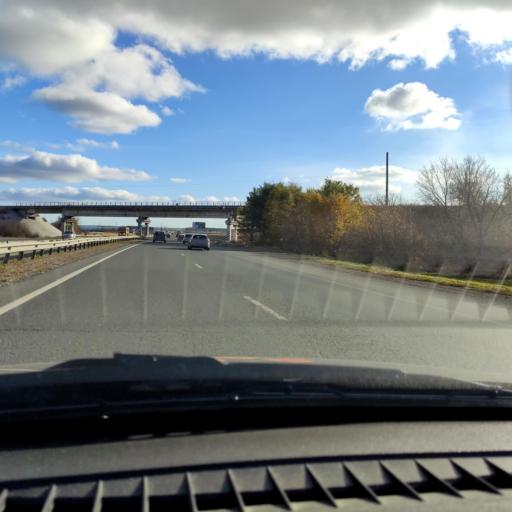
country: RU
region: Samara
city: Tol'yatti
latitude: 53.5640
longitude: 49.4961
